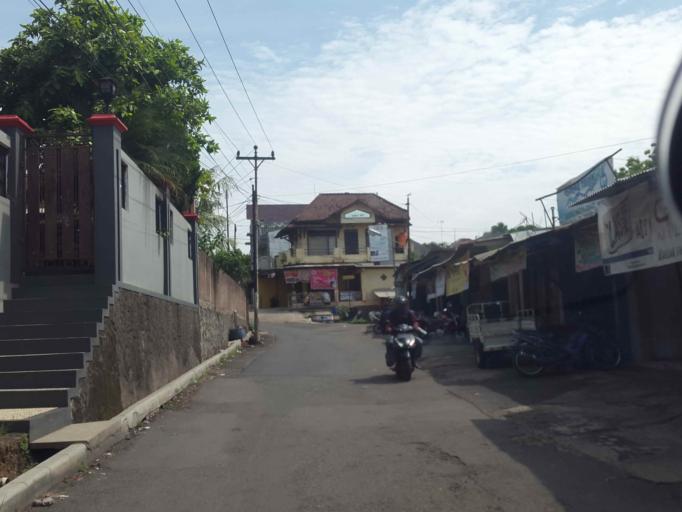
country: ID
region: Central Java
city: Semarang
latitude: -7.0067
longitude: 110.3698
